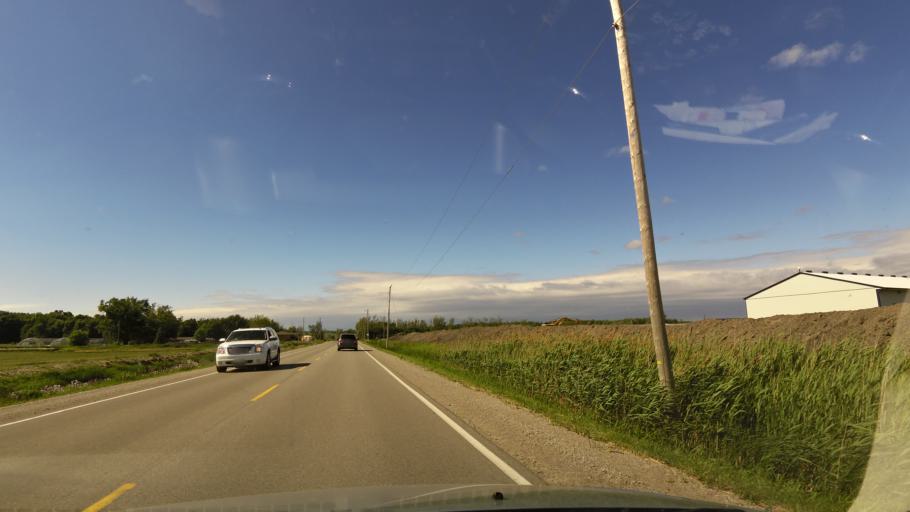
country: CA
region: Ontario
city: Innisfil
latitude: 44.2291
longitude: -79.6342
